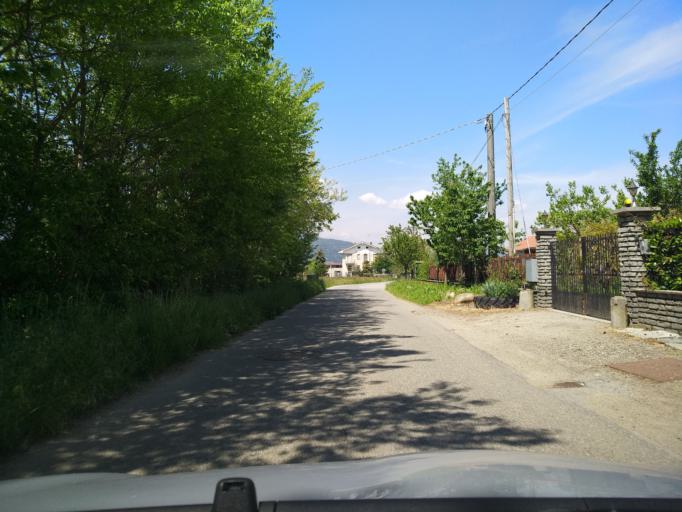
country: IT
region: Piedmont
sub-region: Provincia di Torino
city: Frossasco
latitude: 44.9055
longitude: 7.3558
